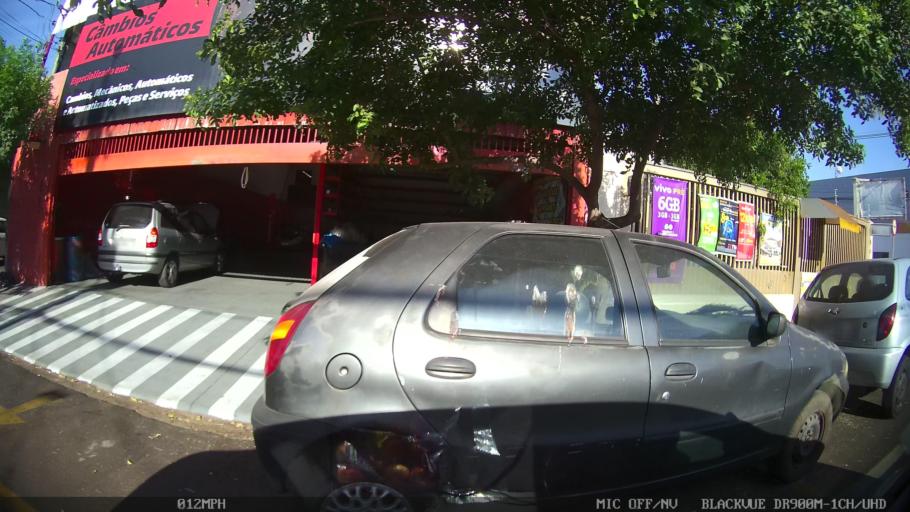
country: BR
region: Sao Paulo
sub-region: Sao Jose Do Rio Preto
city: Sao Jose do Rio Preto
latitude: -20.7902
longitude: -49.3598
